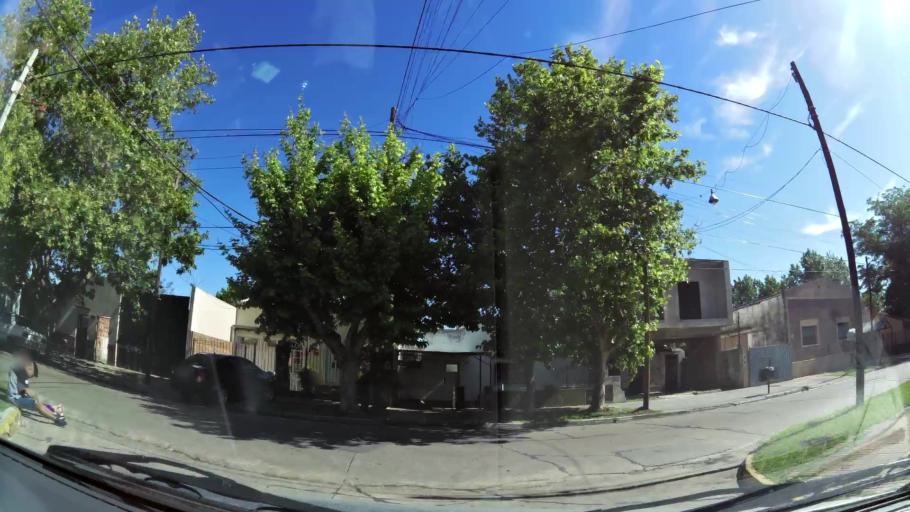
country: AR
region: Buenos Aires
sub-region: Partido de Lomas de Zamora
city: Lomas de Zamora
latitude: -34.7501
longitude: -58.4146
